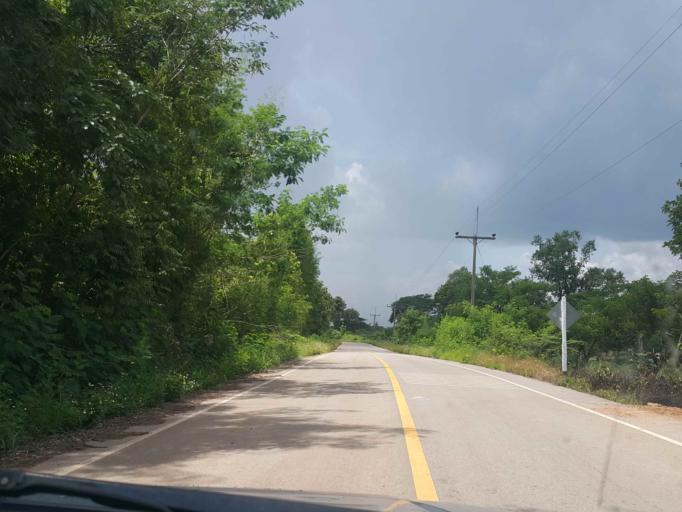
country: TH
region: Phayao
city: Dok Kham Tai
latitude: 19.0491
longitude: 99.9508
